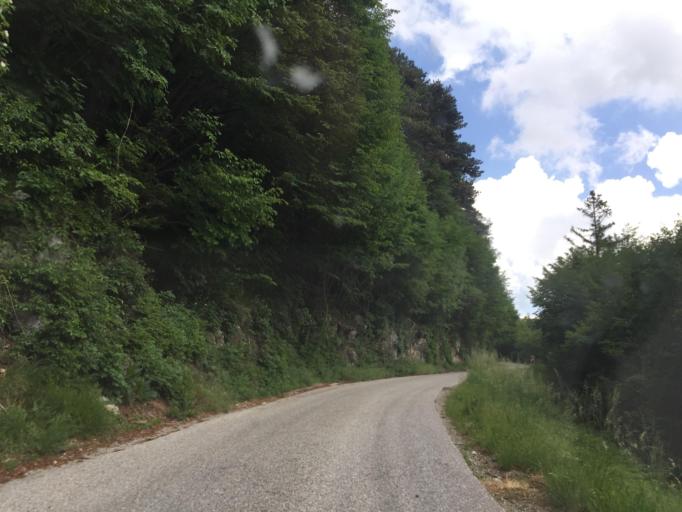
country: SI
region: Nova Gorica
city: Sempas
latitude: 46.0192
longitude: 13.7389
